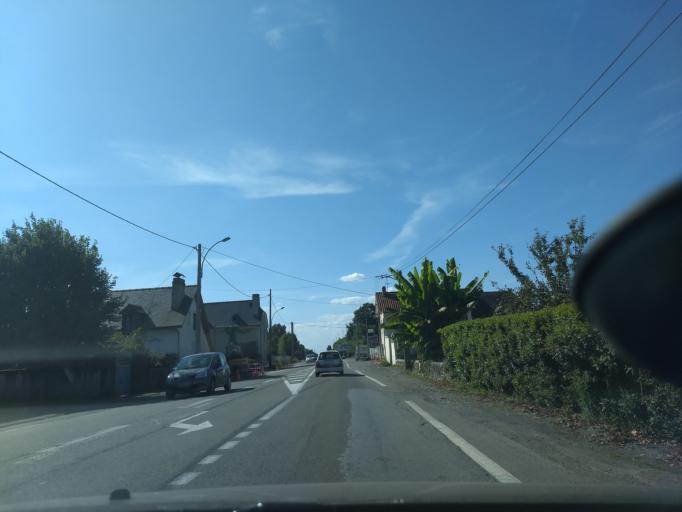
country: FR
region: Aquitaine
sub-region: Departement des Pyrenees-Atlantiques
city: Soumoulou
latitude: 43.2690
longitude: -0.1971
